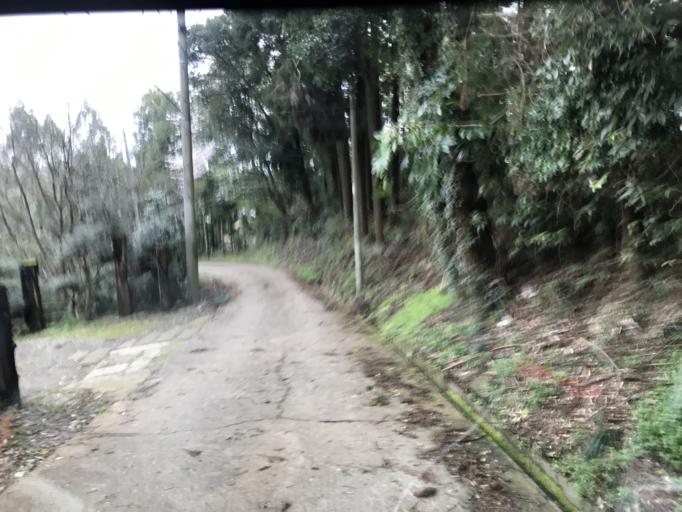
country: JP
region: Chiba
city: Sawara
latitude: 35.8648
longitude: 140.5159
